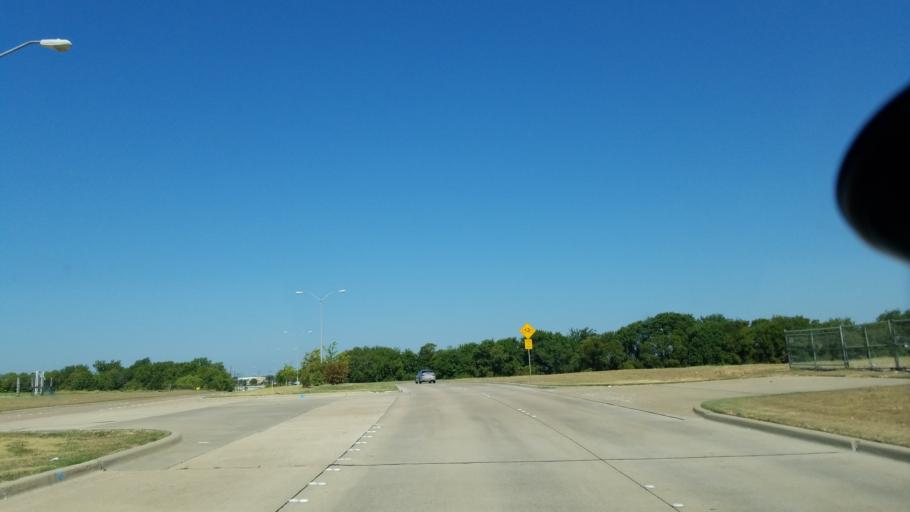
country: US
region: Texas
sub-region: Tarrant County
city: Mansfield
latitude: 32.5699
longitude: -97.1023
